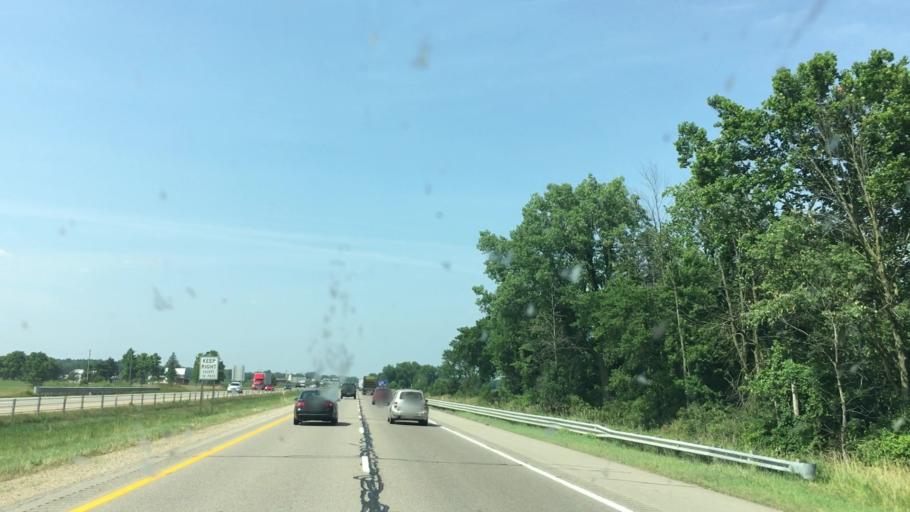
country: US
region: Michigan
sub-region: Allegan County
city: Wayland
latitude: 42.6449
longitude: -85.6620
